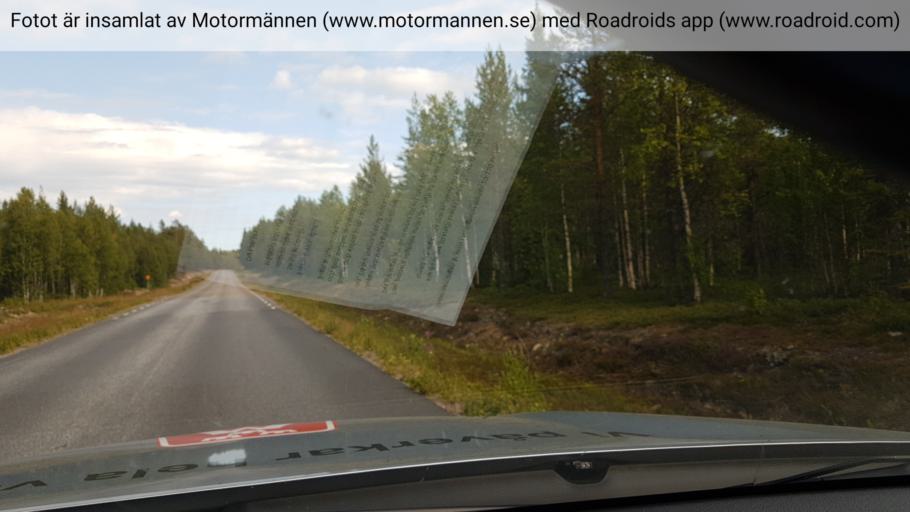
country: SE
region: Vaesterbotten
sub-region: Skelleftea Kommun
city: Boliden
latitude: 65.3168
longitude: 20.2897
